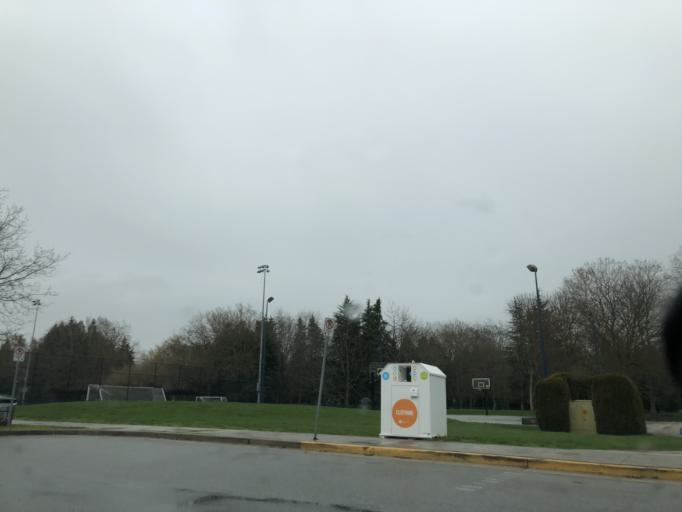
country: CA
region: British Columbia
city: Richmond
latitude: 49.1463
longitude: -123.1782
